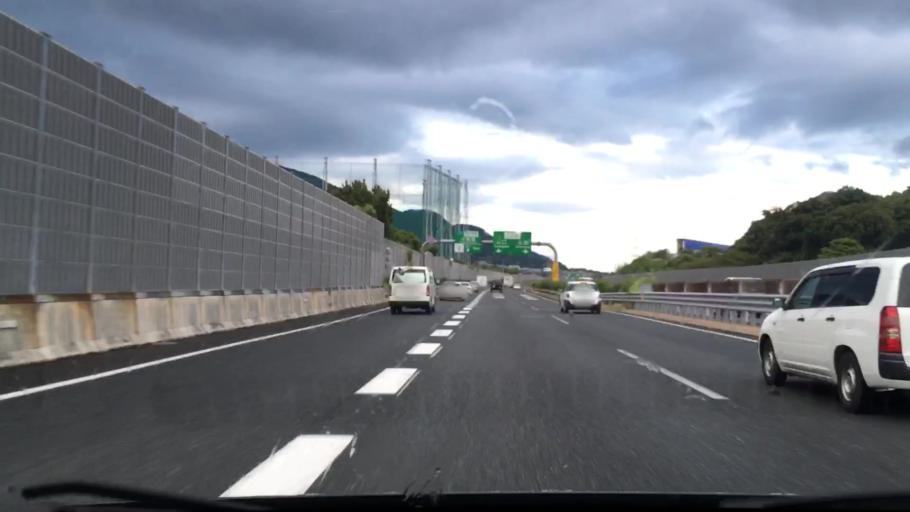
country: JP
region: Fukuoka
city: Kitakyushu
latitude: 33.8278
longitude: 130.8988
